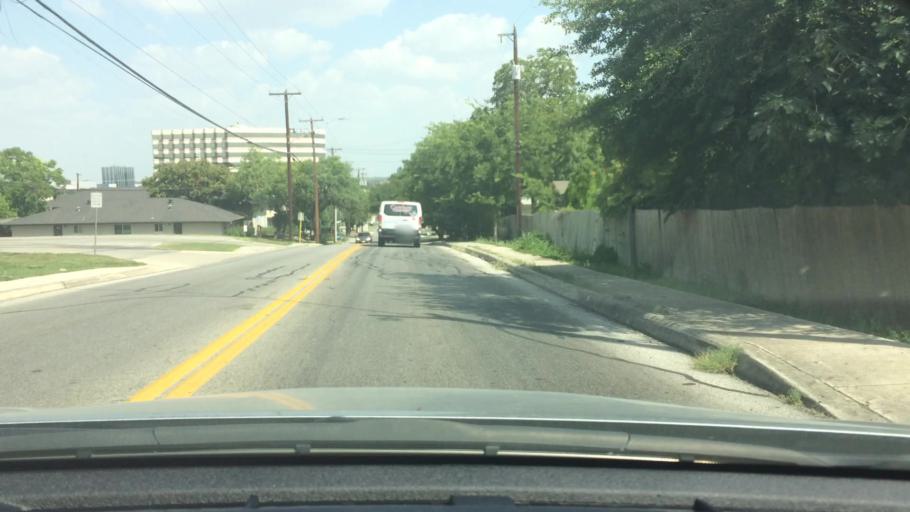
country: US
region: Texas
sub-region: Bexar County
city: Castle Hills
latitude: 29.5330
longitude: -98.4987
